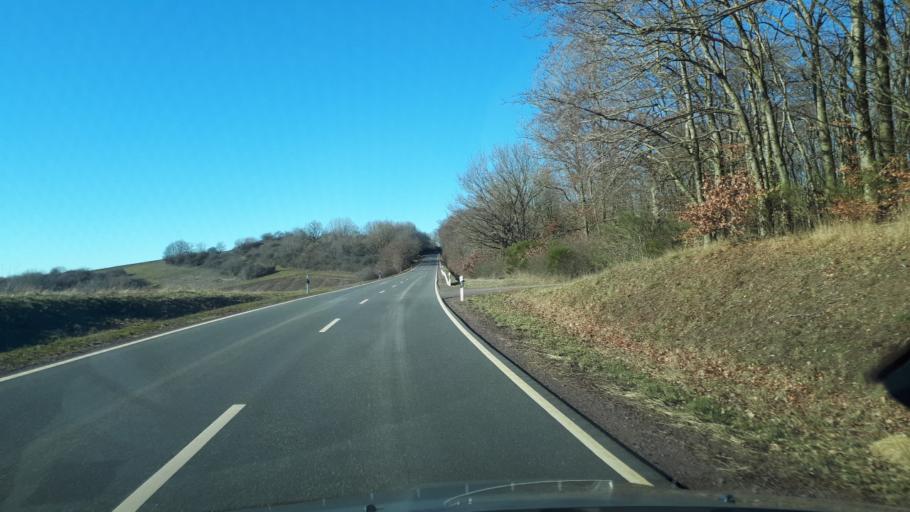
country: DE
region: Rheinland-Pfalz
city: Immerath
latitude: 50.1187
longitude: 6.9593
